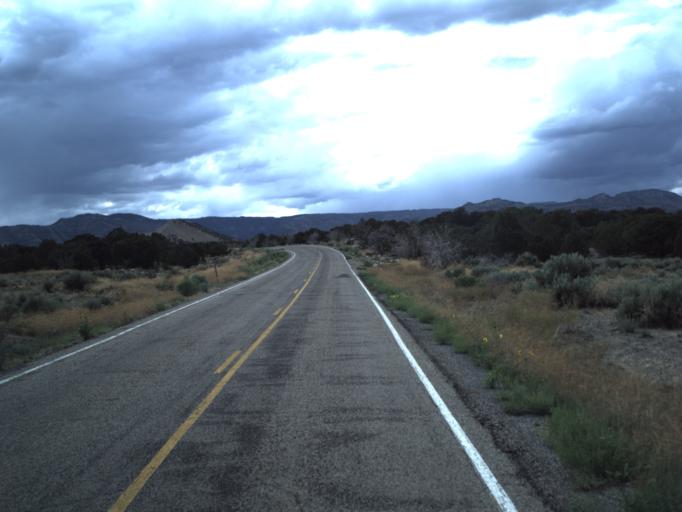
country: US
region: Utah
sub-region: Carbon County
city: Price
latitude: 39.4847
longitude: -110.9069
